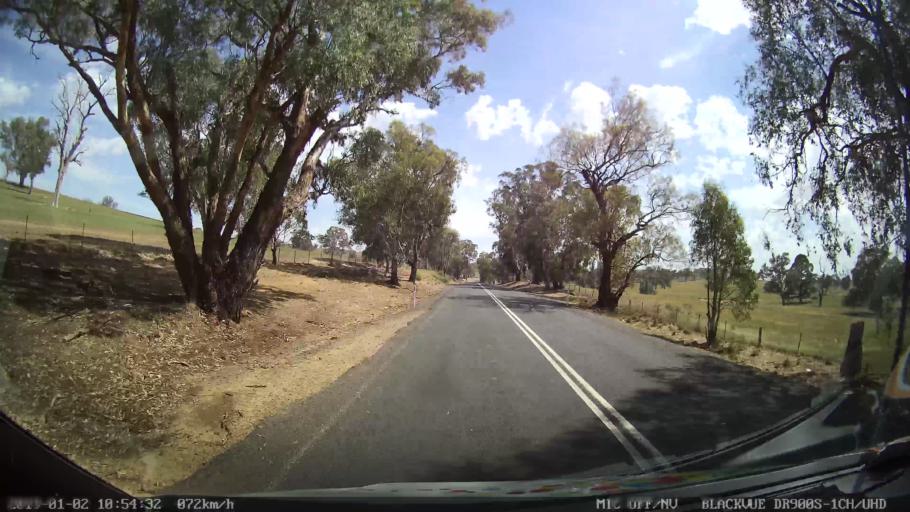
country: AU
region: New South Wales
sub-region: Cootamundra
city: Cootamundra
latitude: -34.6687
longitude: 148.2734
